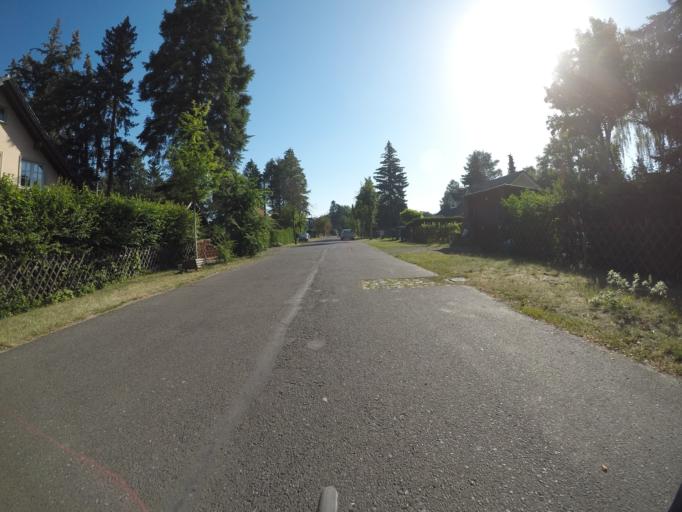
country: DE
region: Berlin
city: Schmockwitz
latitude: 52.3477
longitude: 13.6403
